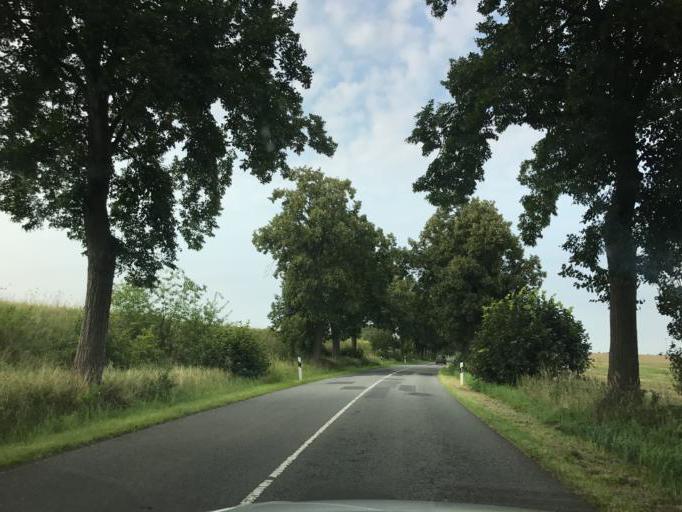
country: DE
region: Mecklenburg-Vorpommern
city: Rechlin
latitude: 53.3207
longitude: 12.7244
